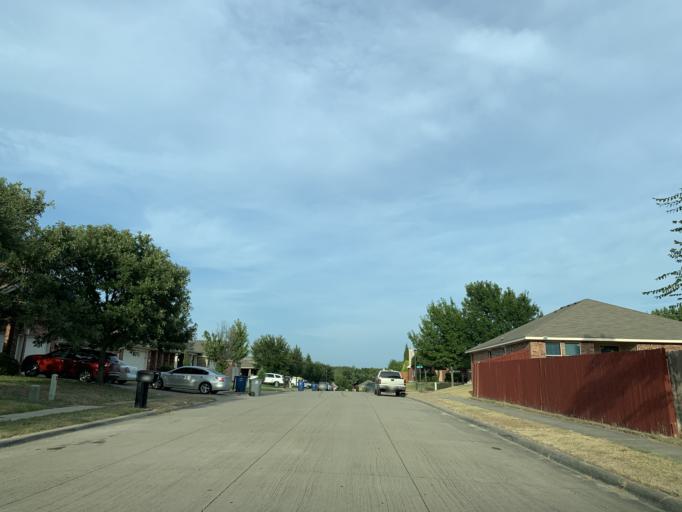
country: US
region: Texas
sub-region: Dallas County
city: Cockrell Hill
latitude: 32.6998
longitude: -96.8950
